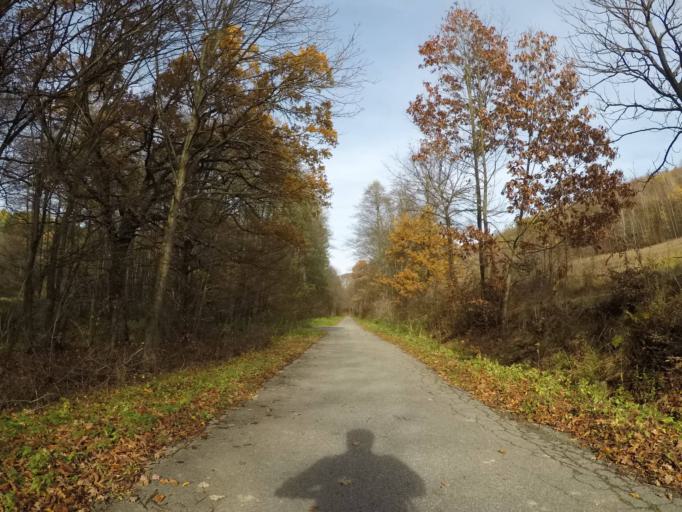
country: SK
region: Presovsky
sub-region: Okres Presov
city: Presov
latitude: 48.9690
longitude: 21.1927
